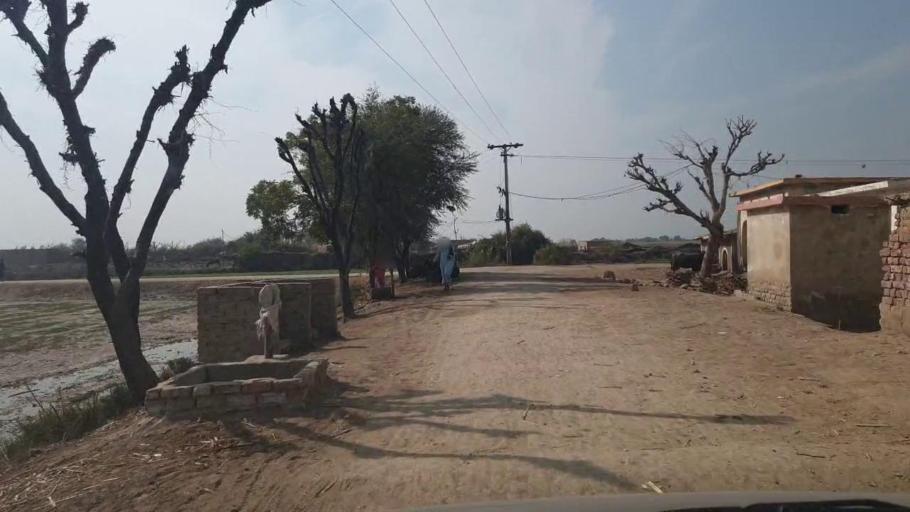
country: PK
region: Sindh
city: Shahdadpur
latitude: 25.8769
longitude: 68.5969
